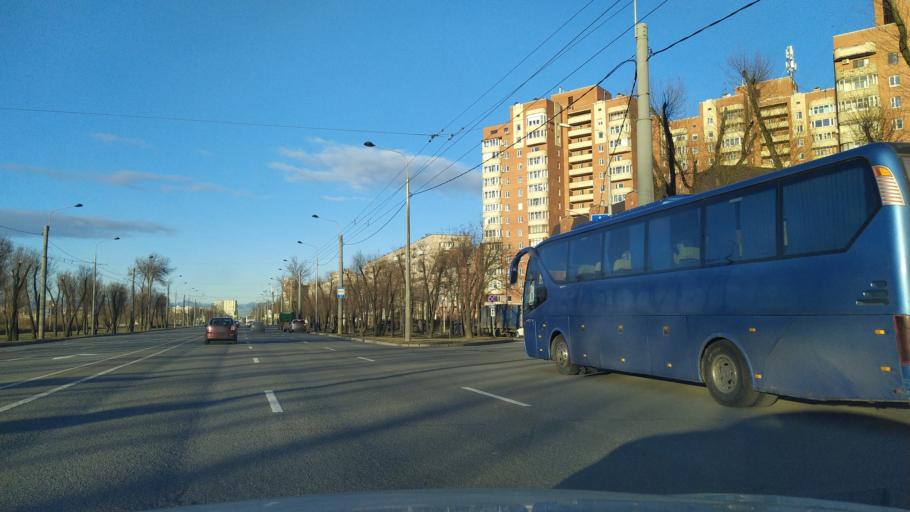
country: RU
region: St.-Petersburg
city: Uritsk
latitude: 59.8338
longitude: 30.1957
